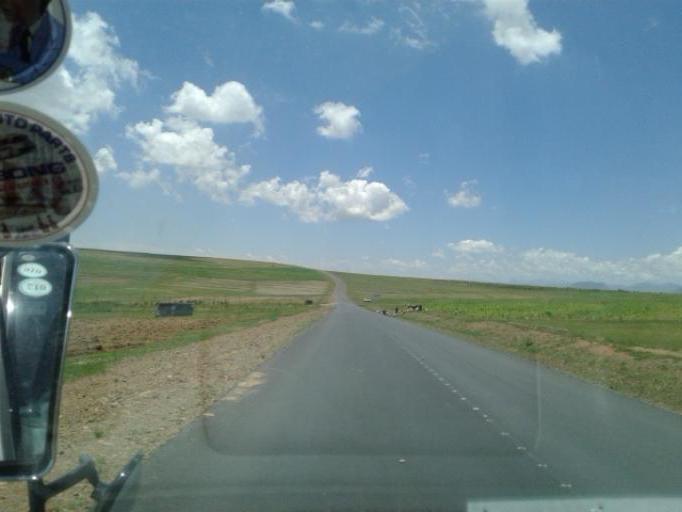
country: LS
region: Maseru
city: Maseru
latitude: -29.3083
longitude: 27.6027
